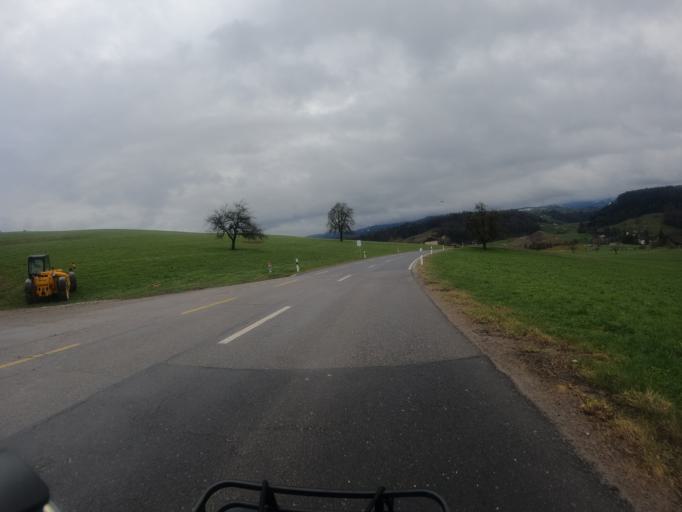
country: CH
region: Zurich
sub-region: Bezirk Affoltern
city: Hausen am Albis / Hausen (Dorf)
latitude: 47.2214
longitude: 8.5578
